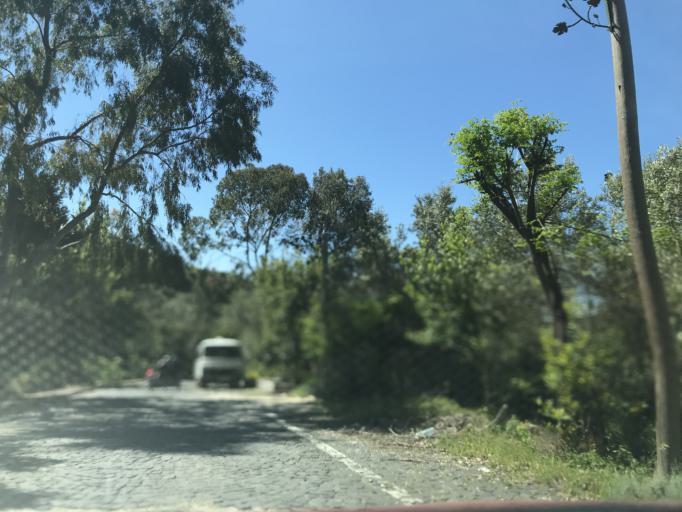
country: TR
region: Hatay
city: Samandag
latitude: 36.1326
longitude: 35.9763
